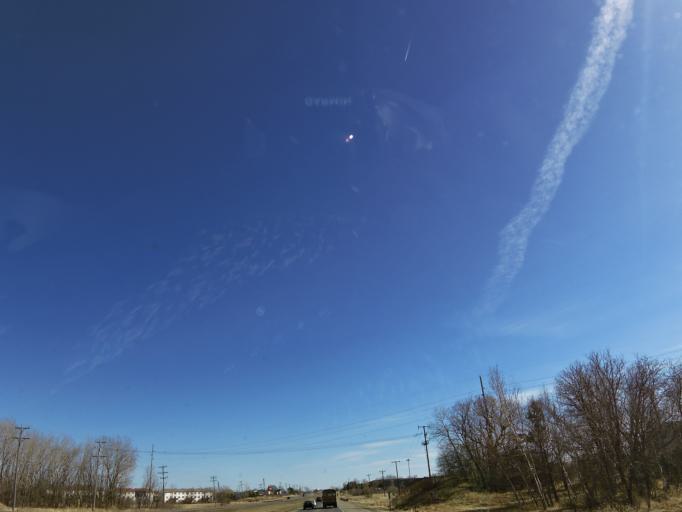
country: US
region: Minnesota
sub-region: Hennepin County
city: Plymouth
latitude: 45.0282
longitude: -93.5022
